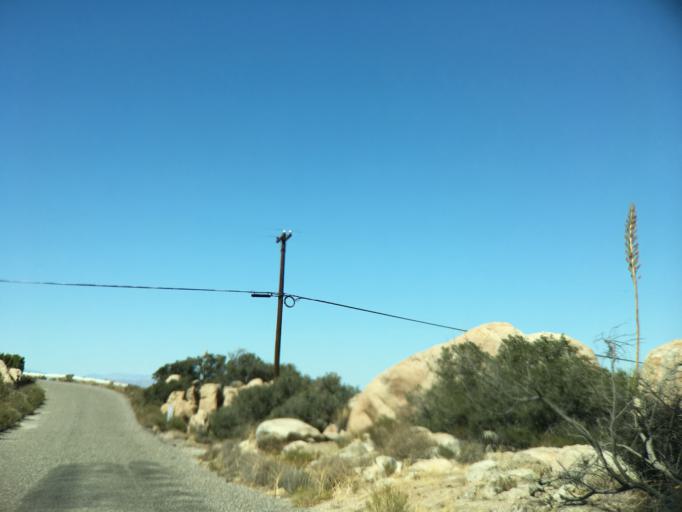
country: MX
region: Baja California
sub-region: Tecate
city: Cereso del Hongo
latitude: 32.6575
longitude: -116.0988
